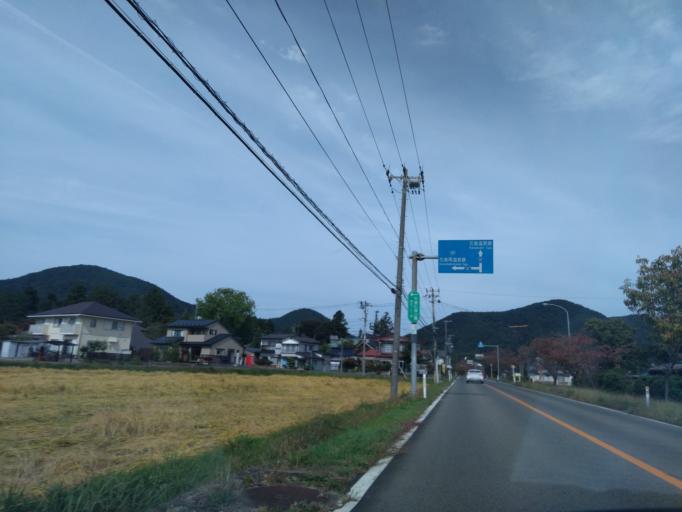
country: JP
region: Iwate
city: Hanamaki
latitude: 39.4429
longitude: 141.0766
